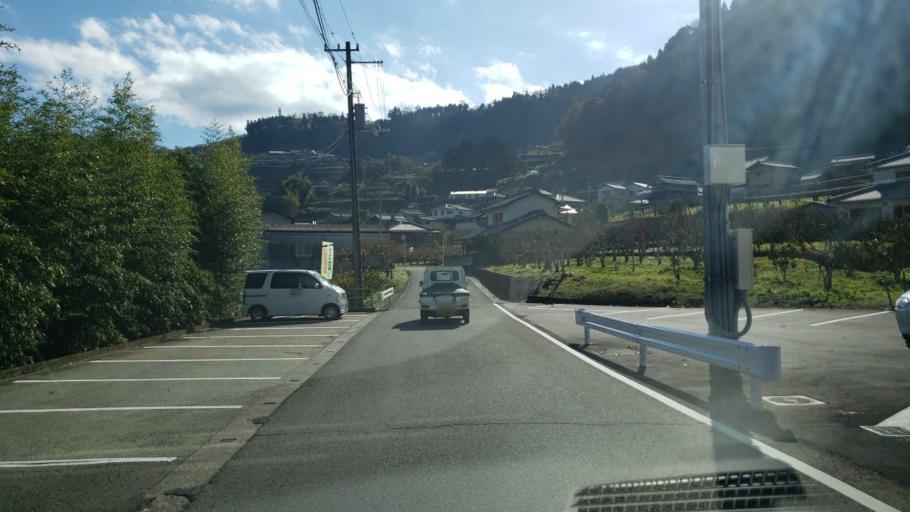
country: JP
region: Tokushima
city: Wakimachi
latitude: 34.0260
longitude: 134.0294
